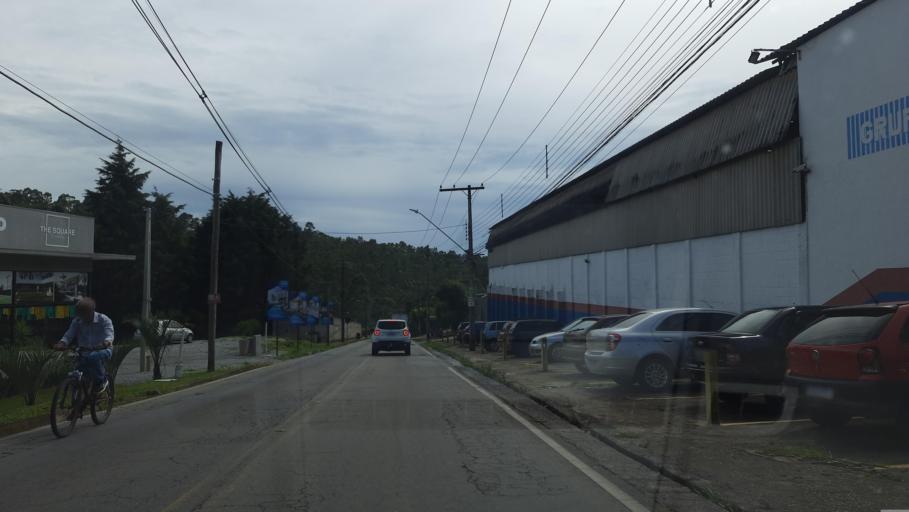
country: BR
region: Sao Paulo
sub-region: Caieiras
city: Caieiras
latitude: -23.3776
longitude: -46.7121
